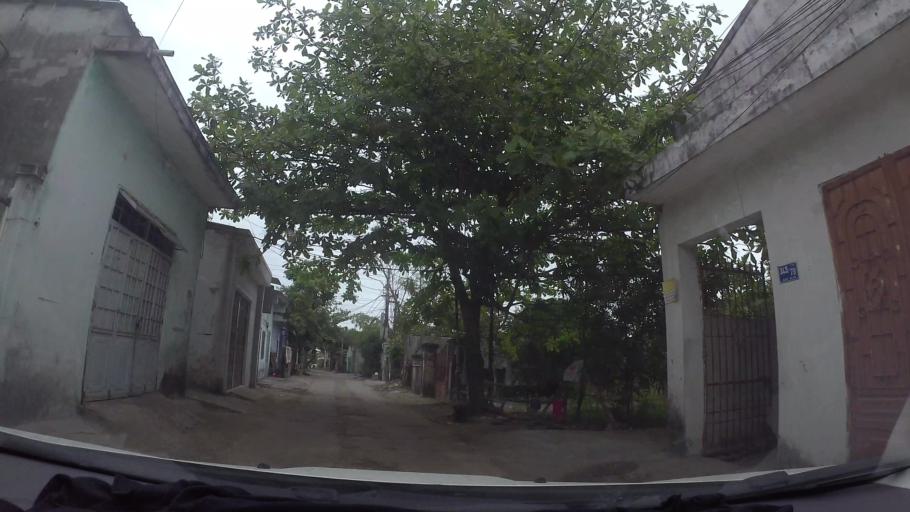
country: VN
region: Da Nang
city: Lien Chieu
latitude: 16.0723
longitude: 108.1367
